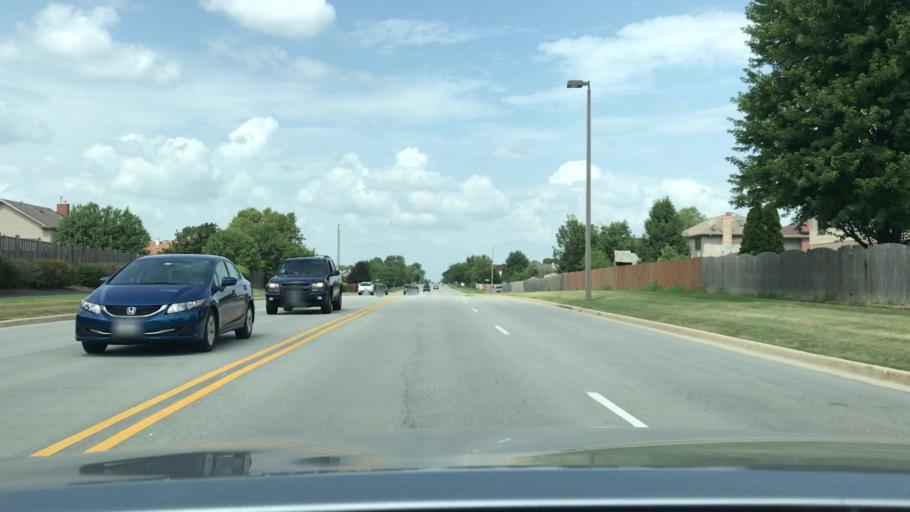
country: US
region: Illinois
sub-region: DuPage County
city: Woodridge
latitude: 41.7379
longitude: -88.0306
